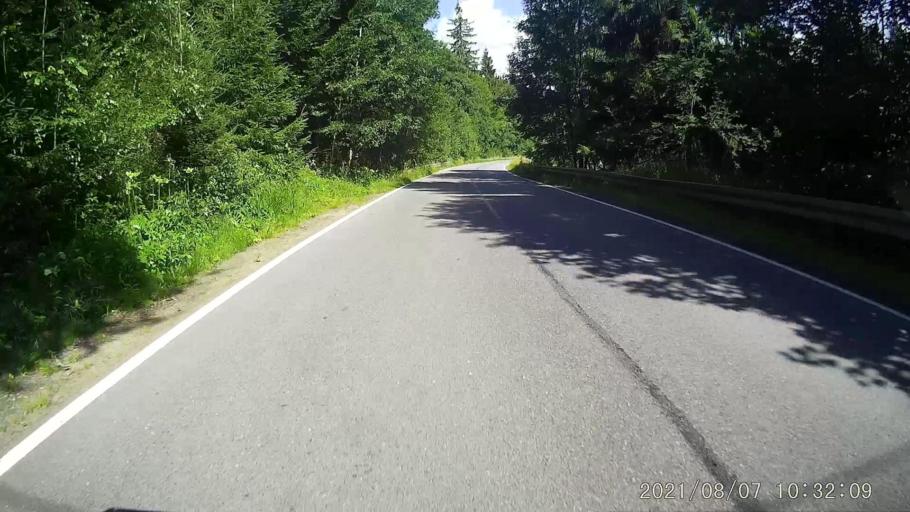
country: PL
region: Lower Silesian Voivodeship
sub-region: Powiat klodzki
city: Duszniki-Zdroj
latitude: 50.3913
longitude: 16.3554
